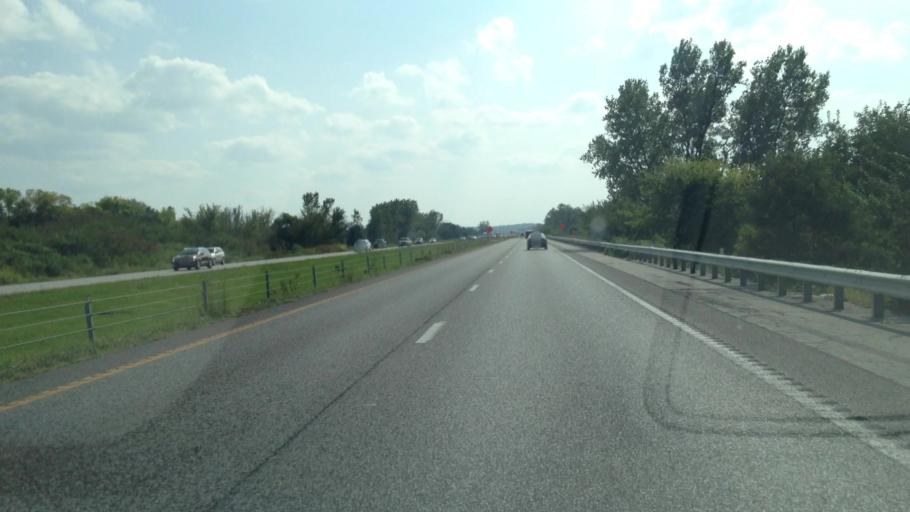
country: US
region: Missouri
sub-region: Clay County
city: Liberty
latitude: 39.3007
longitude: -94.4086
